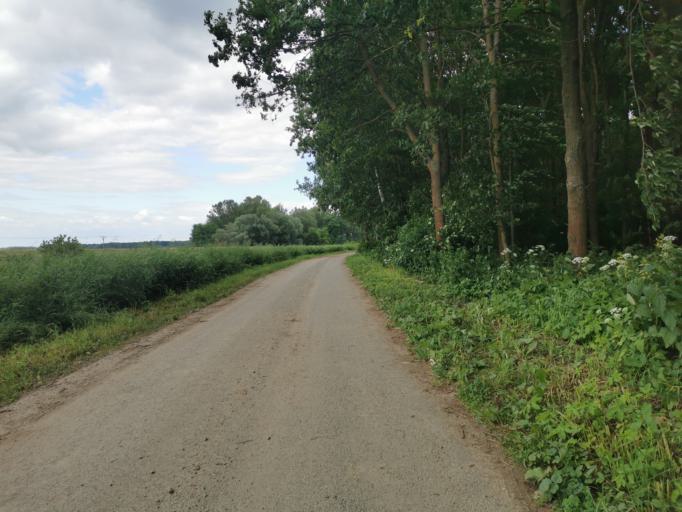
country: CZ
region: South Moravian
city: Straznice
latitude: 48.9347
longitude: 17.3039
